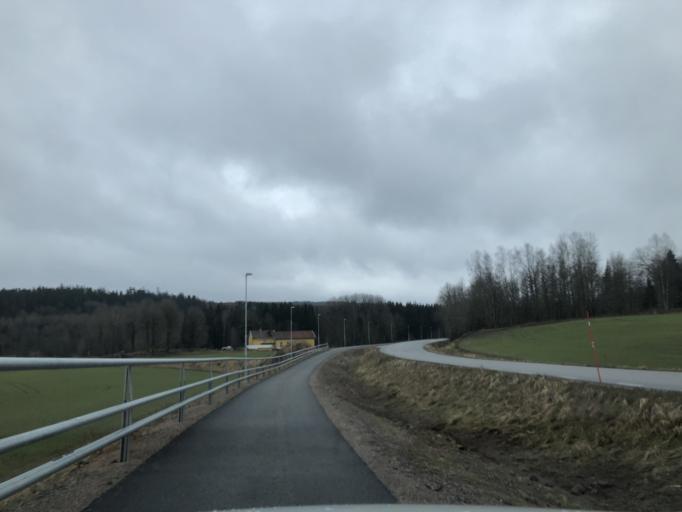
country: SE
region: Vaestra Goetaland
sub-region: Ulricehamns Kommun
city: Ulricehamn
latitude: 57.8341
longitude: 13.2918
